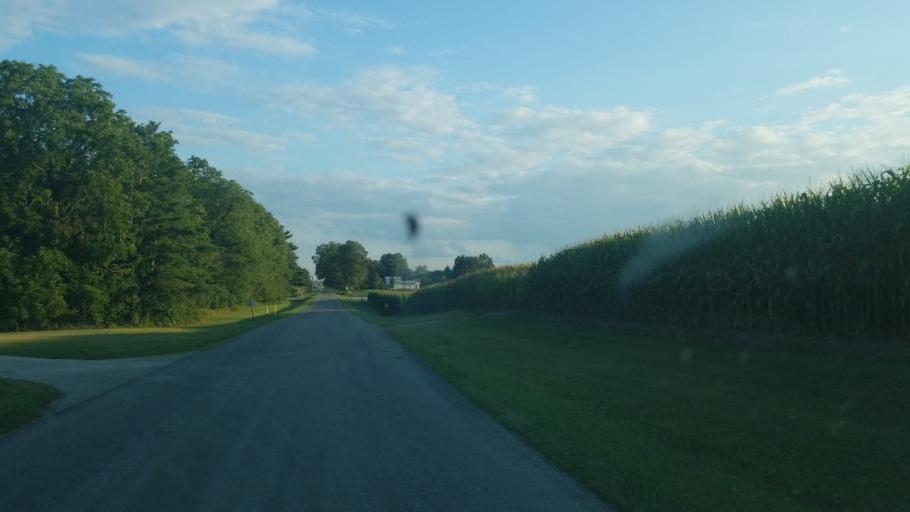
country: US
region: Ohio
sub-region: Huron County
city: Greenwich
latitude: 41.0271
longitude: -82.5599
